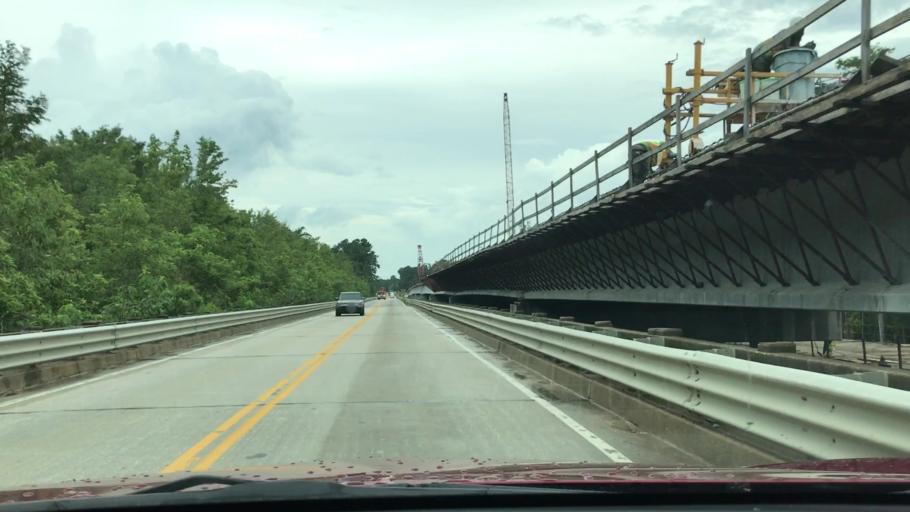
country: US
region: South Carolina
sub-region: Georgetown County
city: Murrells Inlet
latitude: 33.6563
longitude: -79.1604
